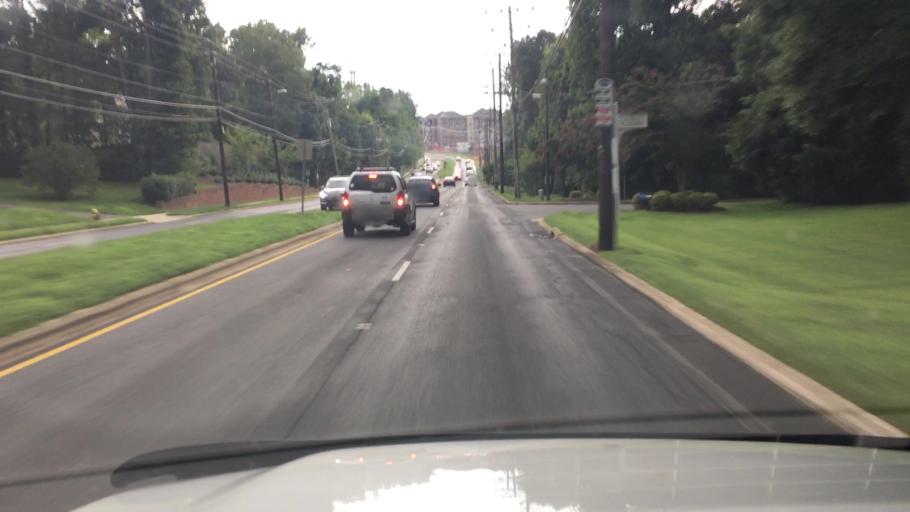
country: US
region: North Carolina
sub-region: Mecklenburg County
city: Charlotte
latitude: 35.1615
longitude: -80.8007
